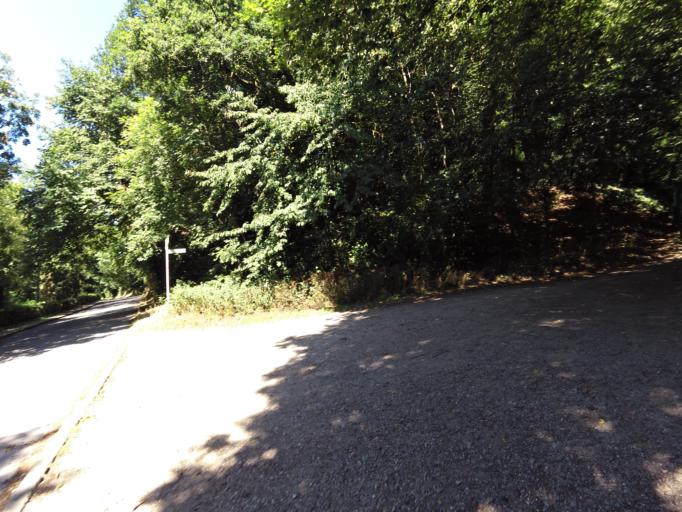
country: DE
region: North Rhine-Westphalia
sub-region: Regierungsbezirk Koln
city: Herzogenrath
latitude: 50.8346
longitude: 6.0973
